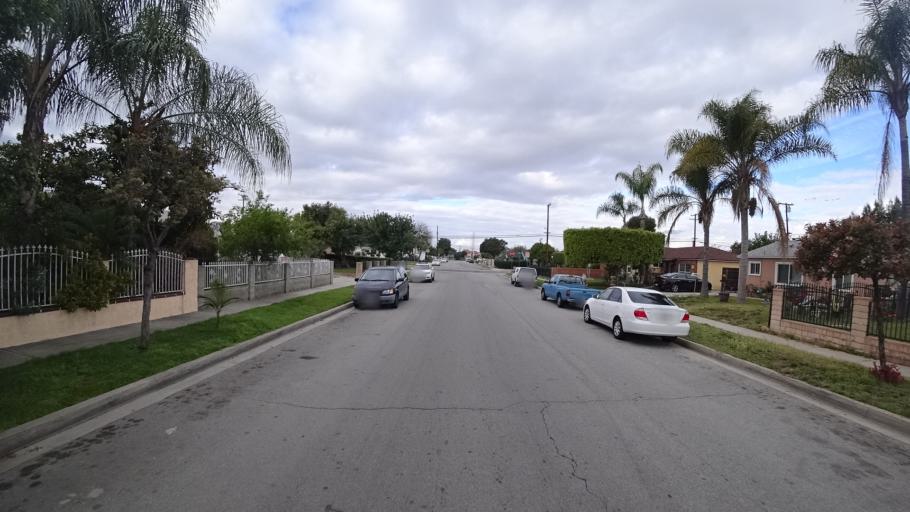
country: US
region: California
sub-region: Los Angeles County
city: Baldwin Park
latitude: 34.1032
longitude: -117.9665
